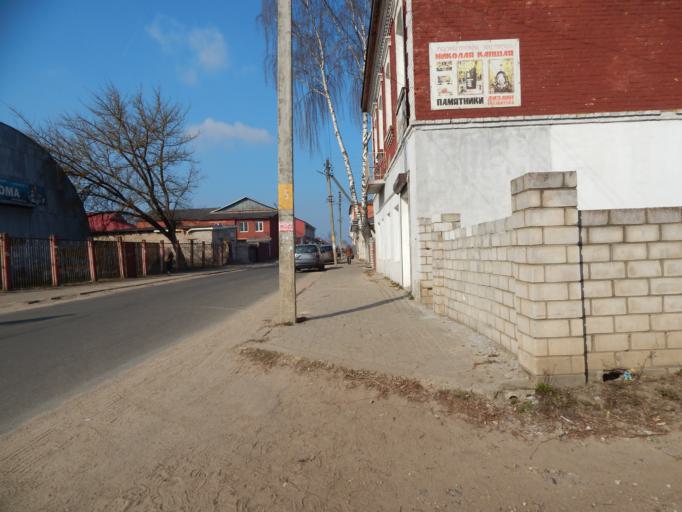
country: BY
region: Minsk
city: Horad Barysaw
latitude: 54.2445
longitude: 28.5072
